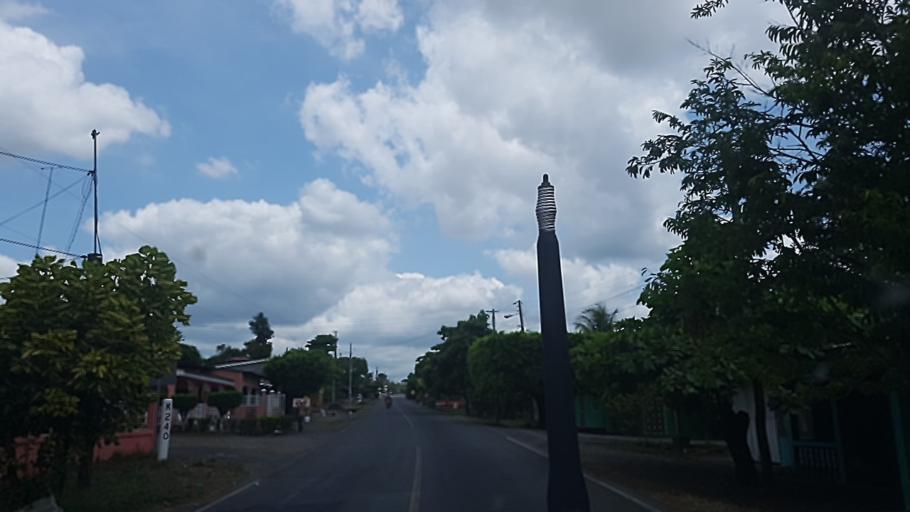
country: NI
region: Atlantico Sur
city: Muelle de los Bueyes
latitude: 11.9163
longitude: -84.6455
